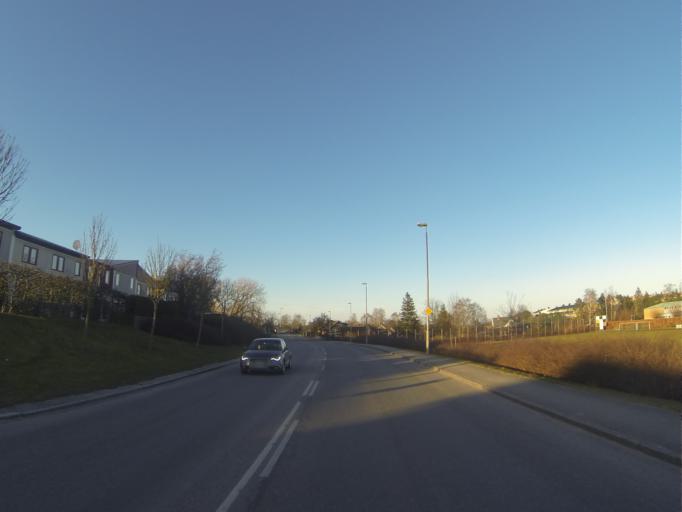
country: SE
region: Skane
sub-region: Malmo
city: Oxie
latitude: 55.5457
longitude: 13.0938
